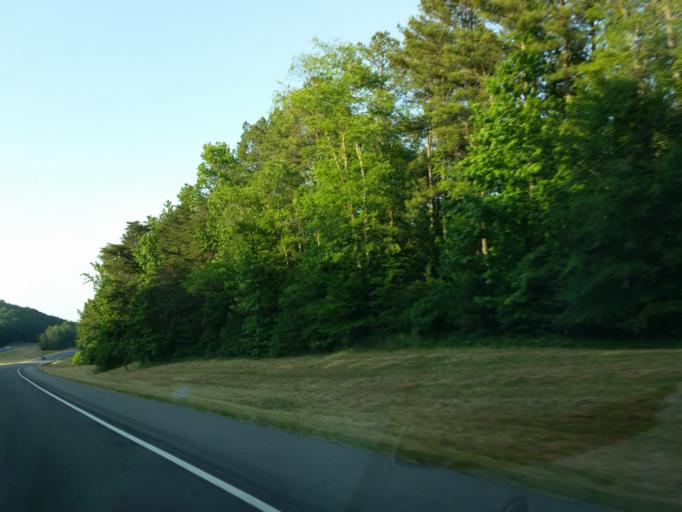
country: US
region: Alabama
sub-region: DeKalb County
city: Henagar
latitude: 34.6137
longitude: -85.6334
